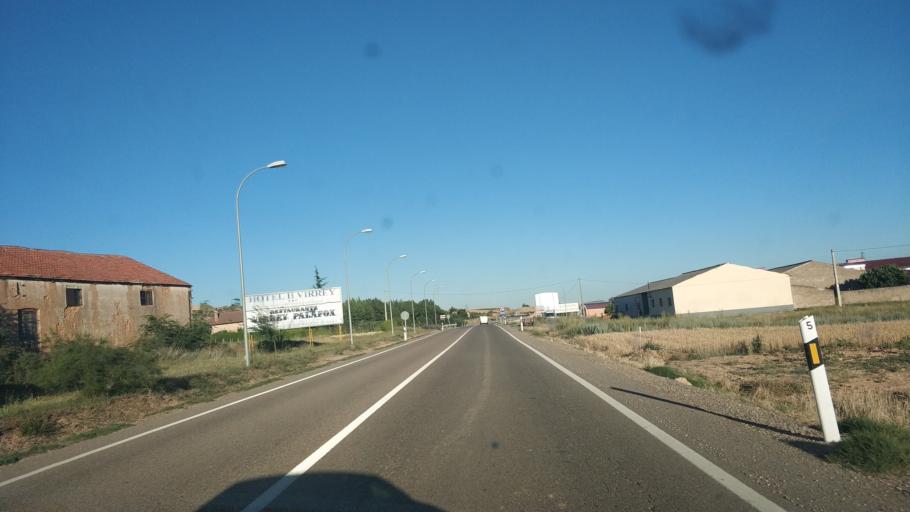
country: ES
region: Castille and Leon
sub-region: Provincia de Soria
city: San Esteban de Gormaz
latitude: 41.5680
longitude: -3.1900
